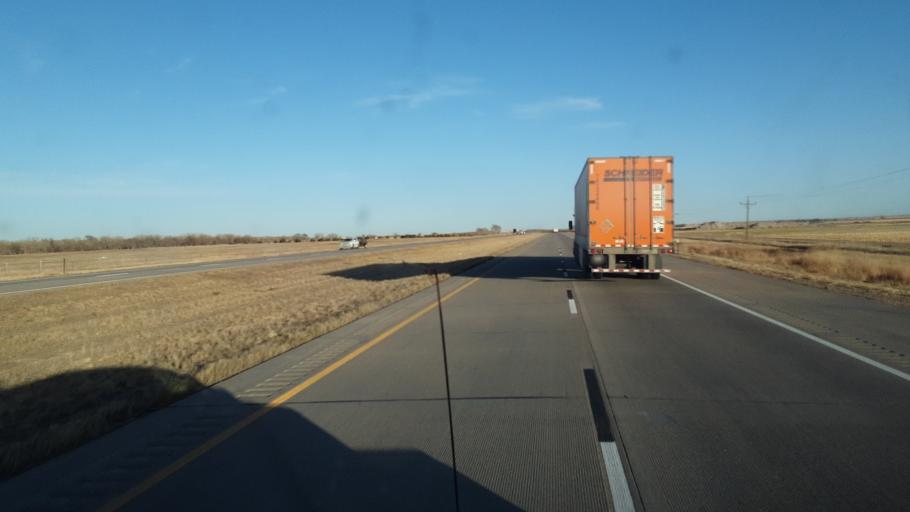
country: US
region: Colorado
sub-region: Sedgwick County
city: Julesburg
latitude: 41.0624
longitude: -102.0066
